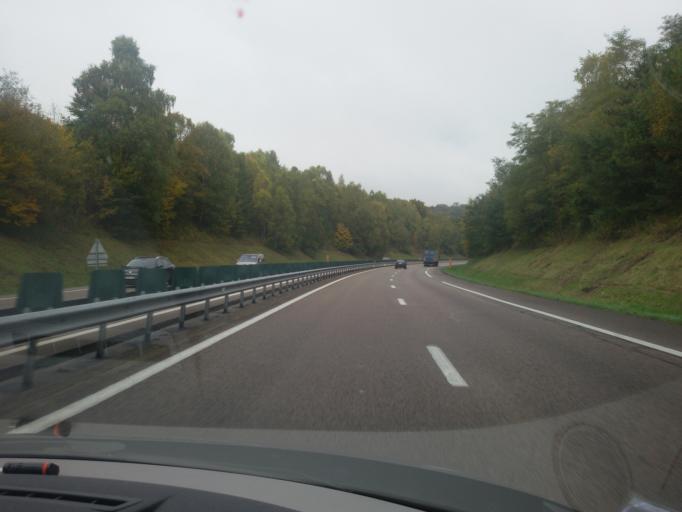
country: FR
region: Haute-Normandie
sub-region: Departement de l'Eure
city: Toutainville
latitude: 49.3769
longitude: 0.4878
